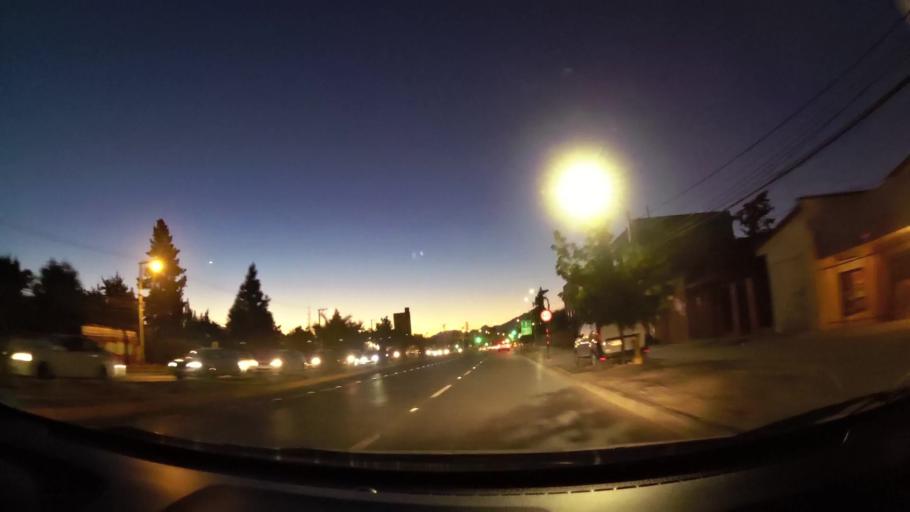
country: CL
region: O'Higgins
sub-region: Provincia de Cachapoal
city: Rancagua
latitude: -34.1748
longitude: -70.7107
